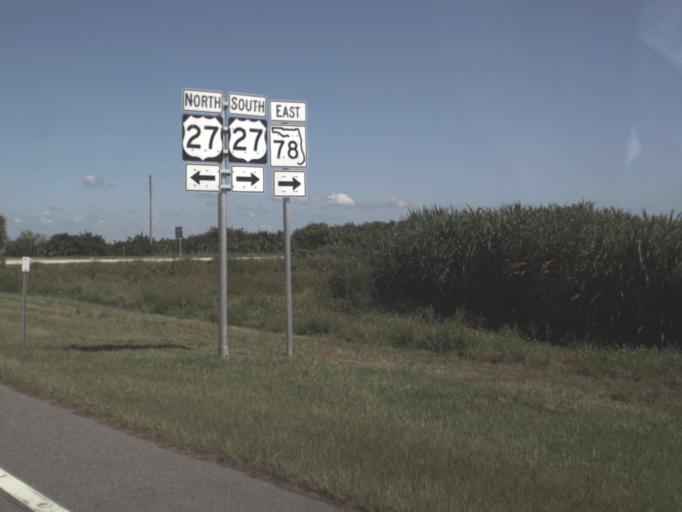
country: US
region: Florida
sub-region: Glades County
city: Moore Haven
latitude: 26.8328
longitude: -81.1870
